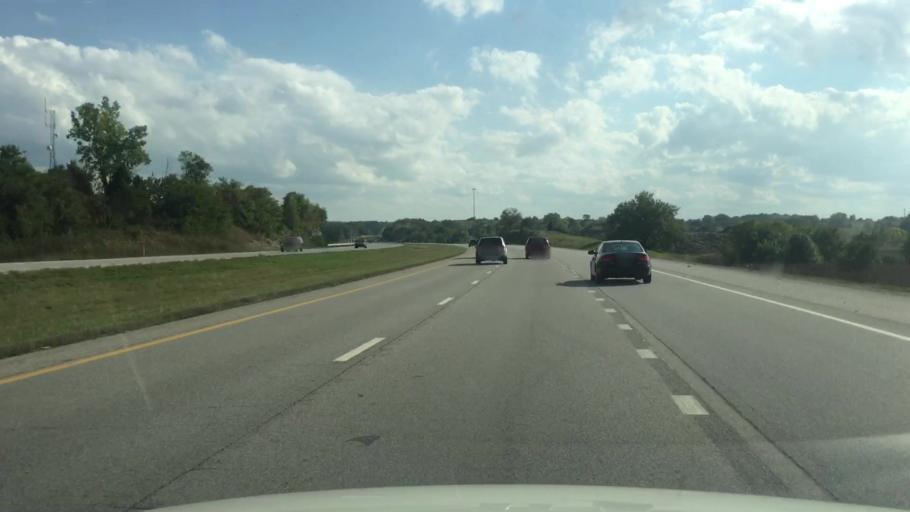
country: US
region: Kansas
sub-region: Johnson County
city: Lenexa
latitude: 38.8319
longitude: -94.6777
